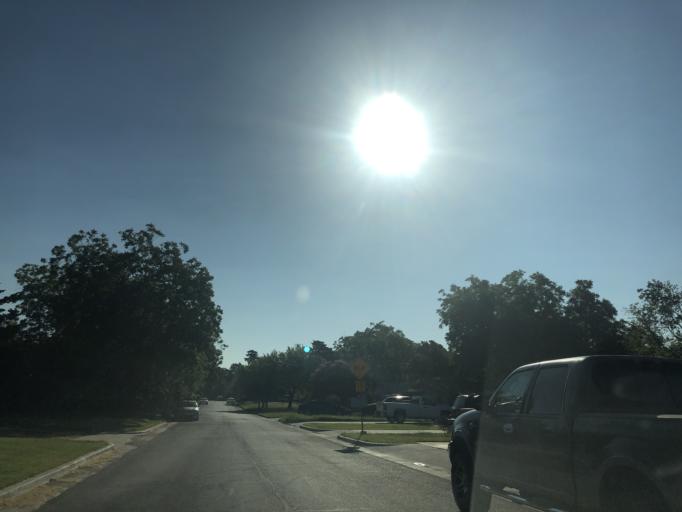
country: US
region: Texas
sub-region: Dallas County
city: Grand Prairie
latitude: 32.7415
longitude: -97.0129
